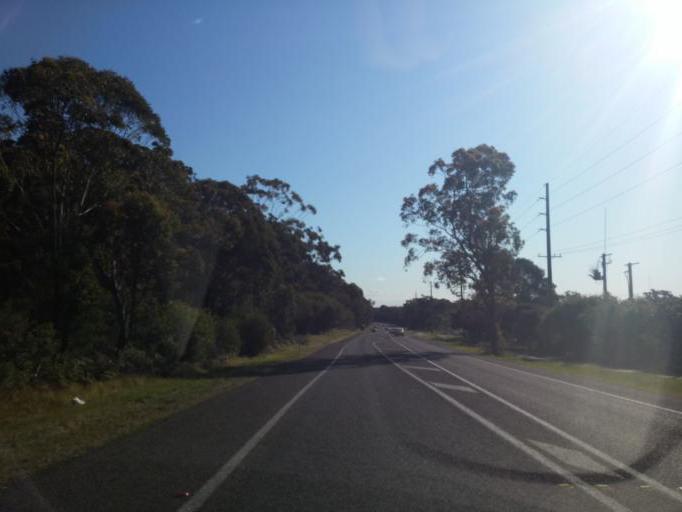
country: AU
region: New South Wales
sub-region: Port Stephens Shire
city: Nelson Bay
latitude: -32.7373
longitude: 152.1267
